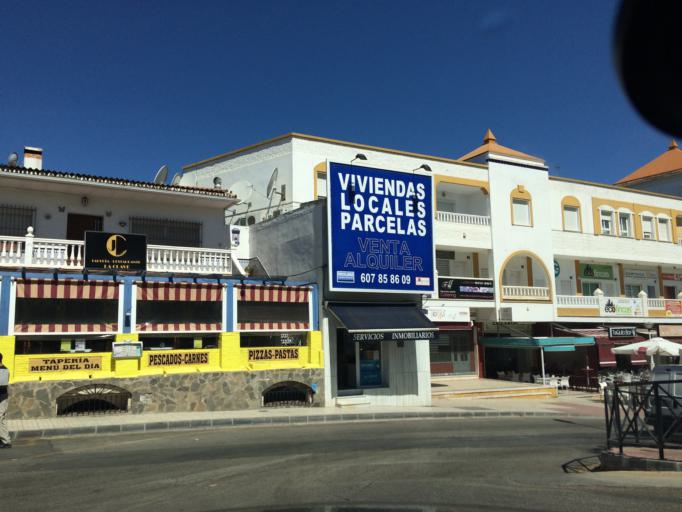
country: ES
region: Andalusia
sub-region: Provincia de Malaga
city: Estacion de Cartama
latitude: 36.7342
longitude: -4.6126
